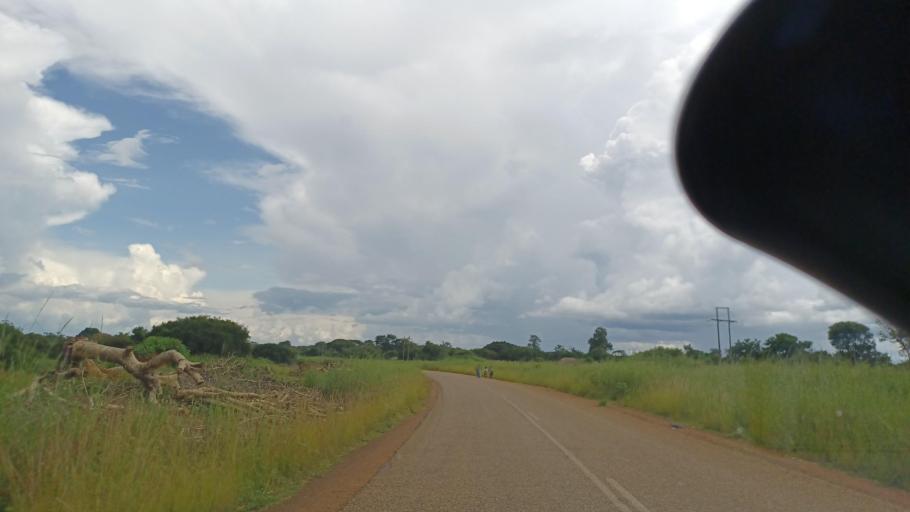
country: ZM
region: North-Western
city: Kasempa
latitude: -13.1218
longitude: 25.8705
